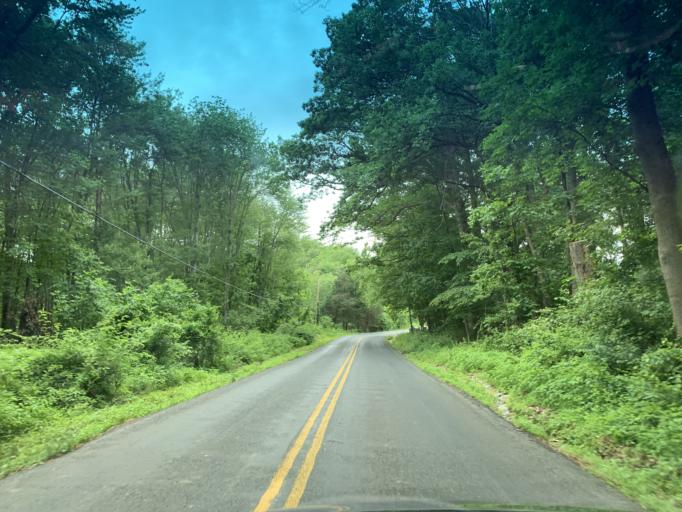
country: US
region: Maryland
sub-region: Harford County
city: Jarrettsville
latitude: 39.6193
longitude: -76.5004
